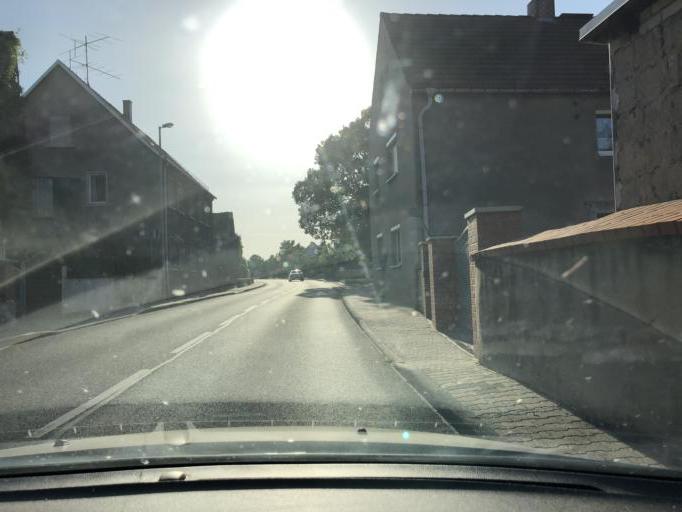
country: DE
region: Saxony
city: Dahlen
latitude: 51.3279
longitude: 13.0026
